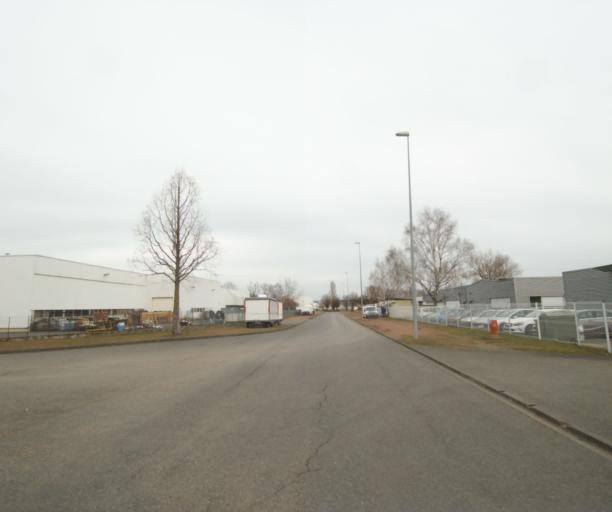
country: FR
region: Rhone-Alpes
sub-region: Departement de la Loire
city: Roanne
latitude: 46.0598
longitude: 4.0795
